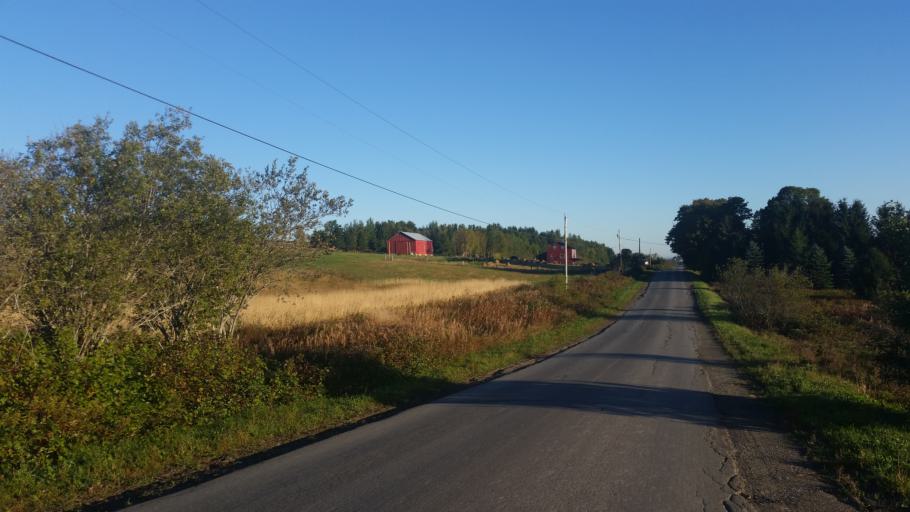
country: US
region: Maine
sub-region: Aroostook County
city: Easton
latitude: 46.6735
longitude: -67.8466
